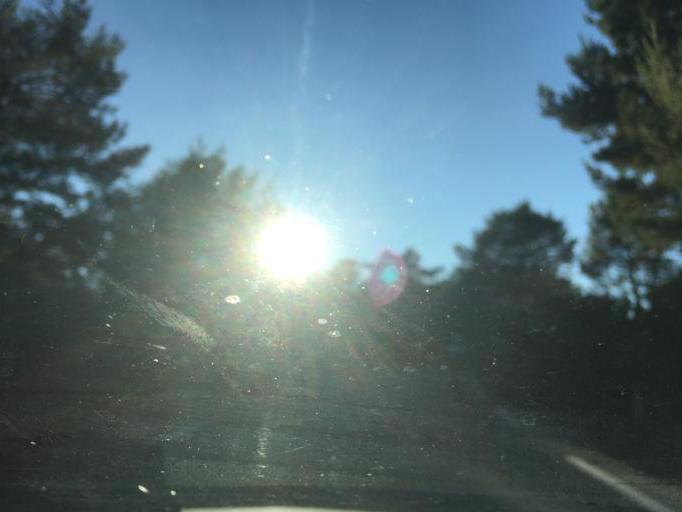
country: FR
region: Provence-Alpes-Cote d'Azur
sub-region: Departement du Var
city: Villecroze
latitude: 43.5984
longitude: 6.3330
